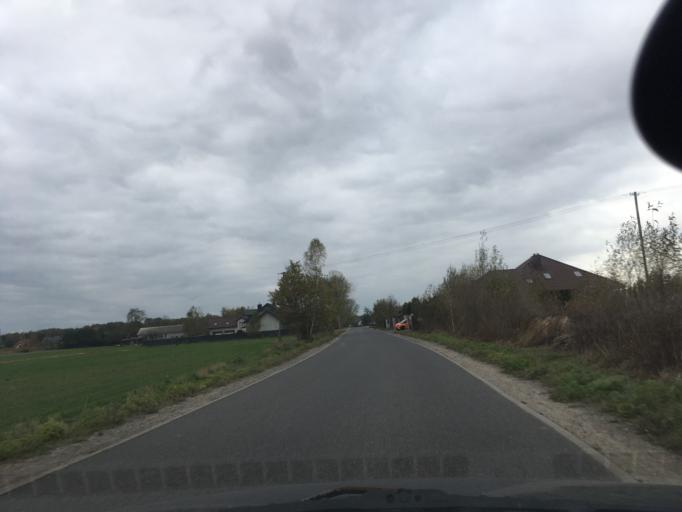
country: PL
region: Lodz Voivodeship
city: Zabia Wola
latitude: 52.0281
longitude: 20.6990
